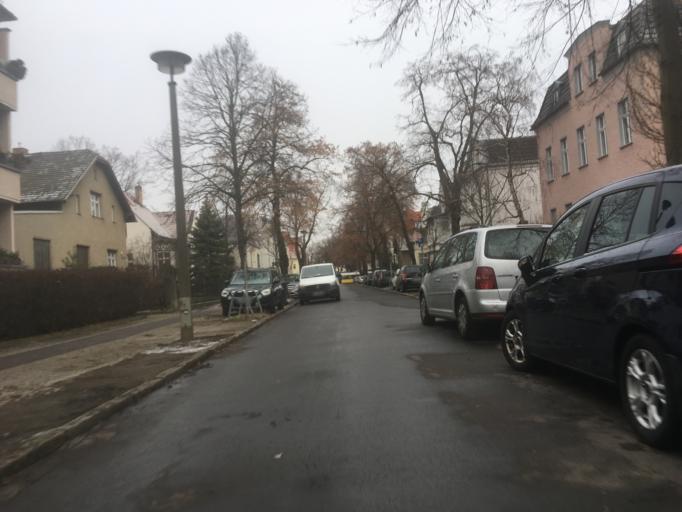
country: DE
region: Berlin
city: Karlshorst
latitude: 52.4795
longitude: 13.5182
